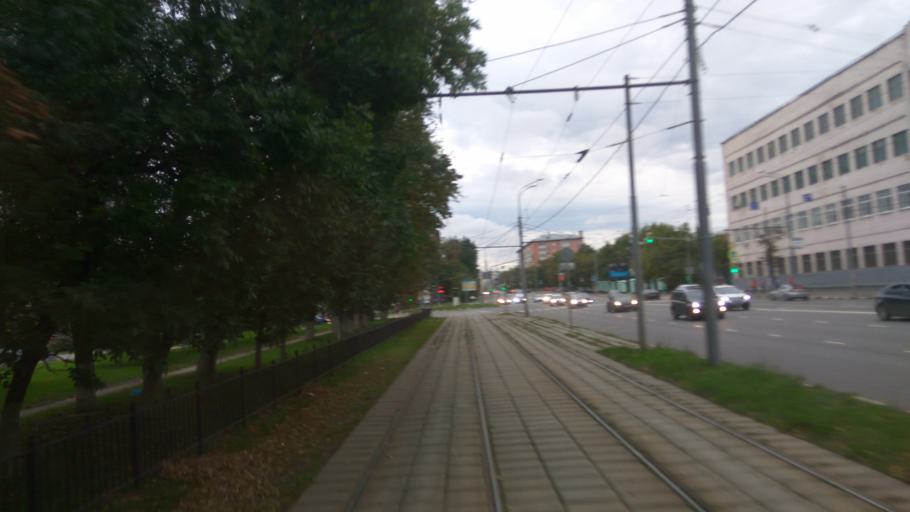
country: RU
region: Moscow
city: Taganskiy
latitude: 55.7200
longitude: 37.6749
